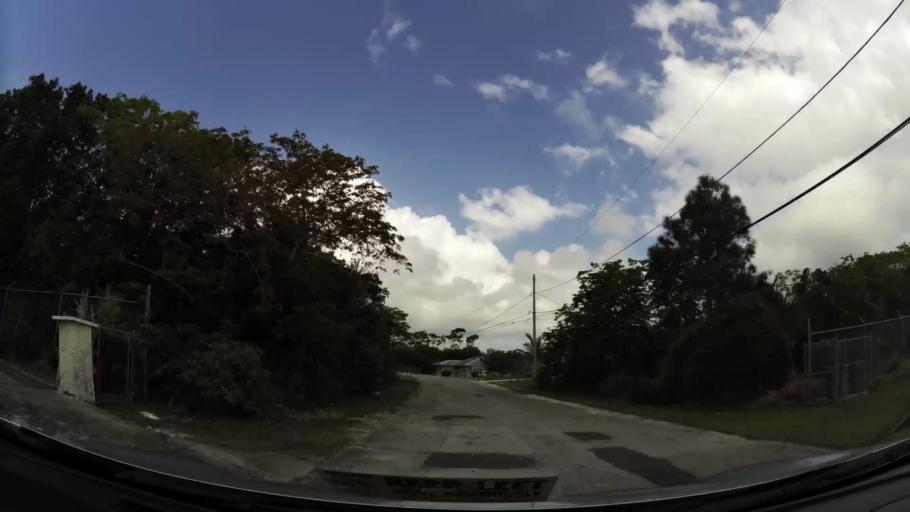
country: BS
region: Freeport
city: Lucaya
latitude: 26.5442
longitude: -78.5887
